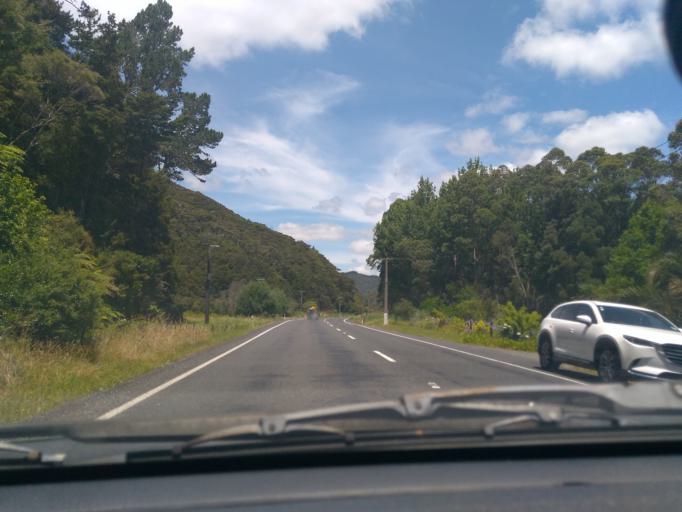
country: NZ
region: Northland
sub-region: Far North District
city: Kerikeri
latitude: -35.0852
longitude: 173.7644
